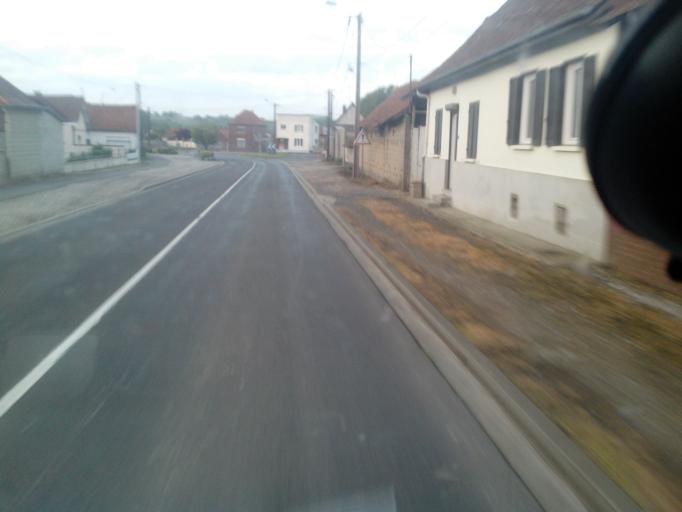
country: FR
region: Picardie
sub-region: Departement de la Somme
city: Crecy-en-Ponthieu
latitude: 50.2688
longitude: 1.9836
